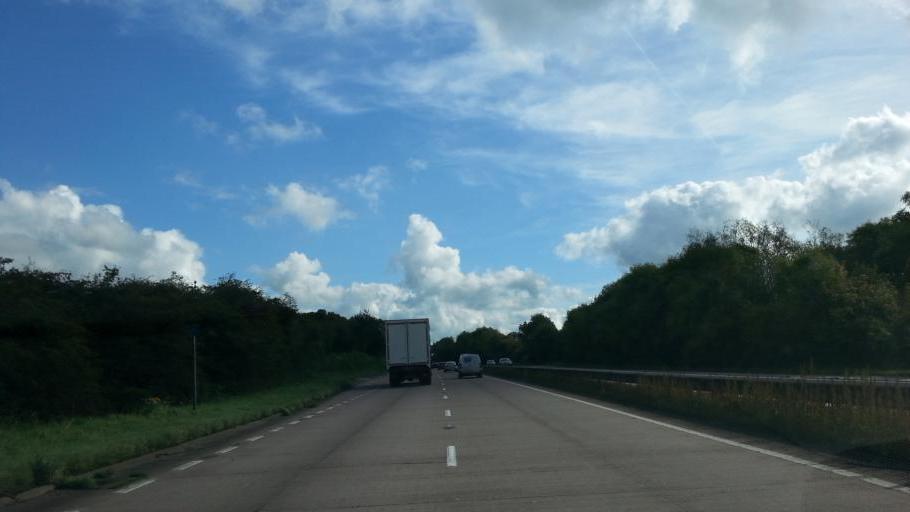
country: GB
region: England
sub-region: Staffordshire
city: Cheadle
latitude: 52.9444
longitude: -2.0055
